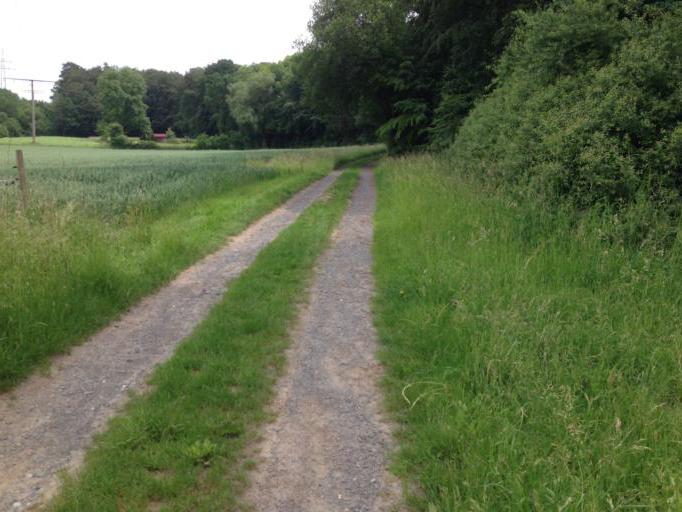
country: DE
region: Hesse
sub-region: Regierungsbezirk Giessen
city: Alten Buseck
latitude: 50.5917
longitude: 8.7450
